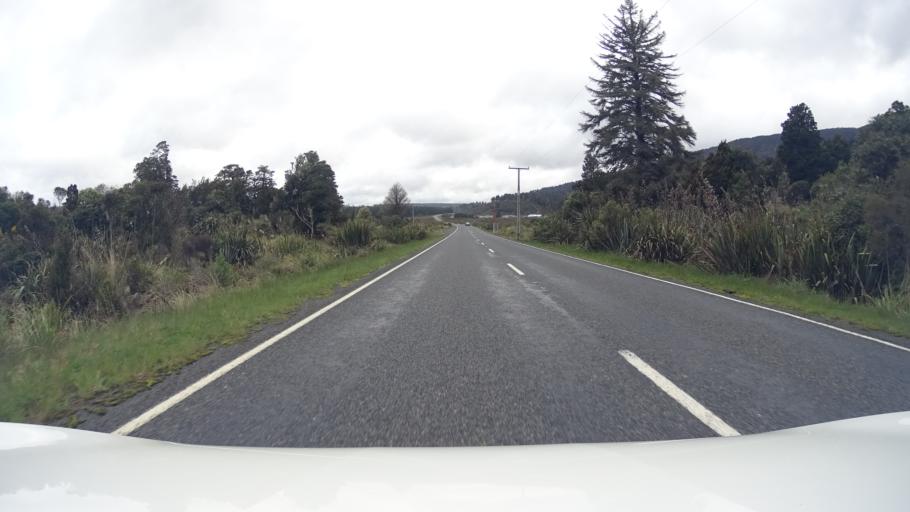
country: NZ
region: Manawatu-Wanganui
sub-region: Ruapehu District
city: Waiouru
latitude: -39.2346
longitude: 175.3924
